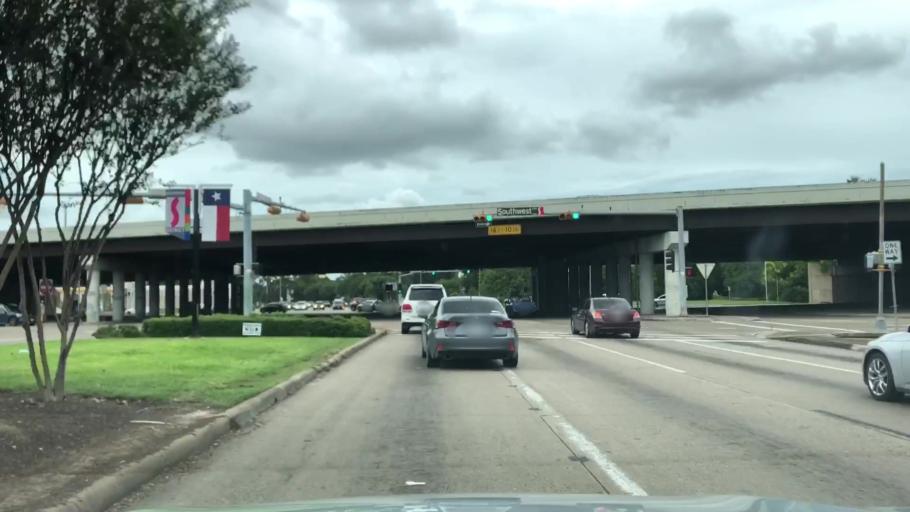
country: US
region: Texas
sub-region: Harris County
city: Bellaire
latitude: 29.7047
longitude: -95.5139
